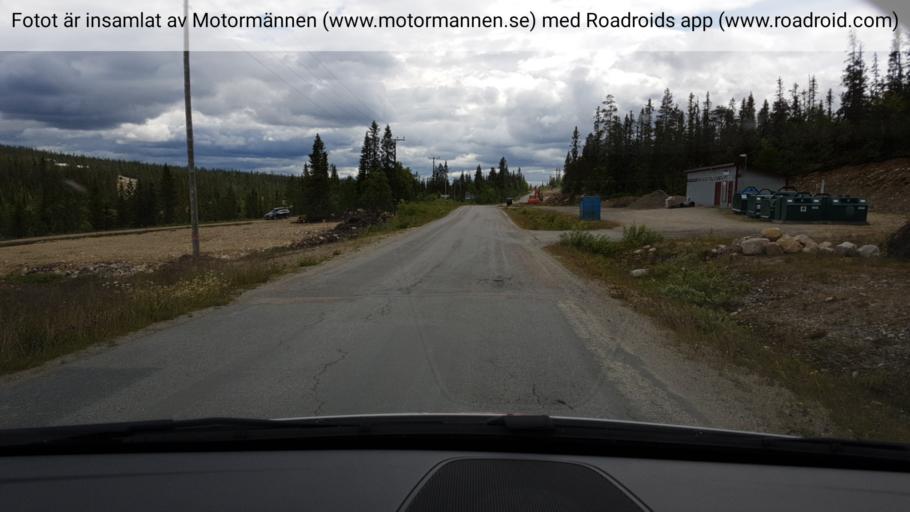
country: SE
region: Jaemtland
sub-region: Bergs Kommun
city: Hoverberg
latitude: 62.5014
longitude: 14.1089
